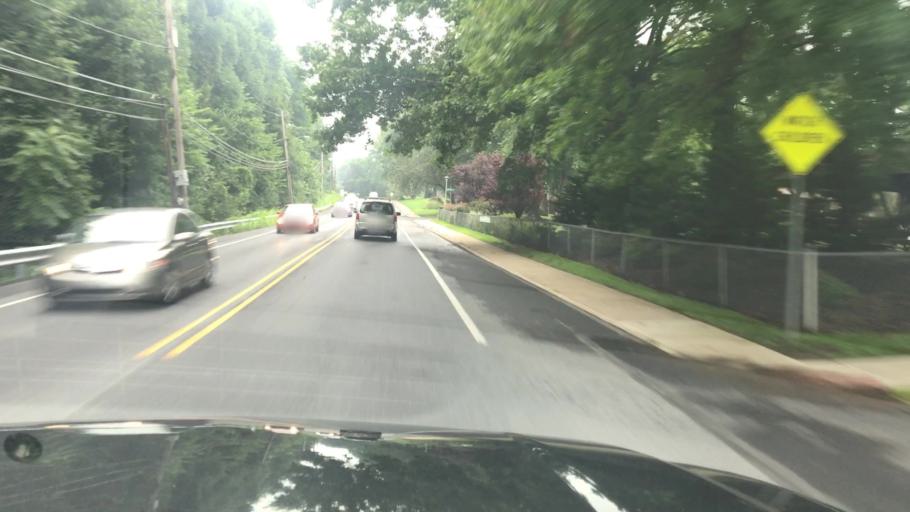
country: US
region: Pennsylvania
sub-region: Cumberland County
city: Shiremanstown
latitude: 40.2455
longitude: -76.9550
